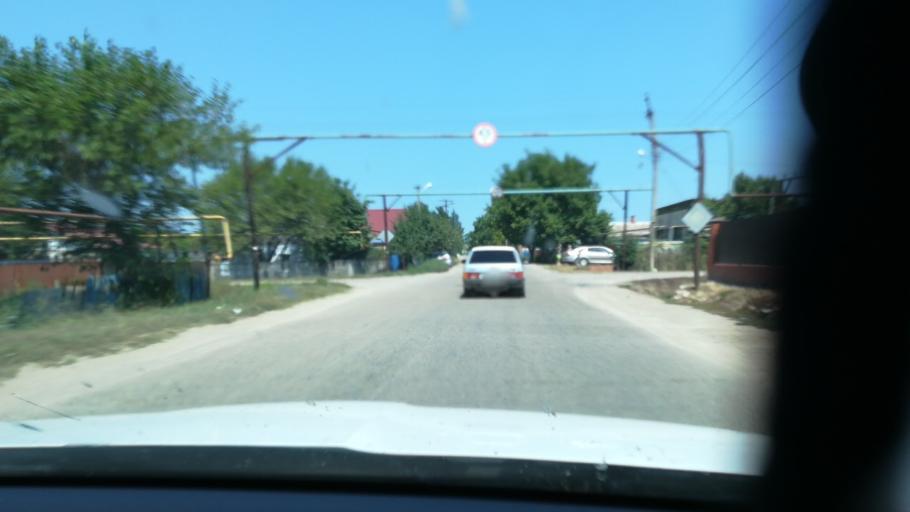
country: RU
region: Krasnodarskiy
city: Starotitarovskaya
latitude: 45.2133
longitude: 37.1439
